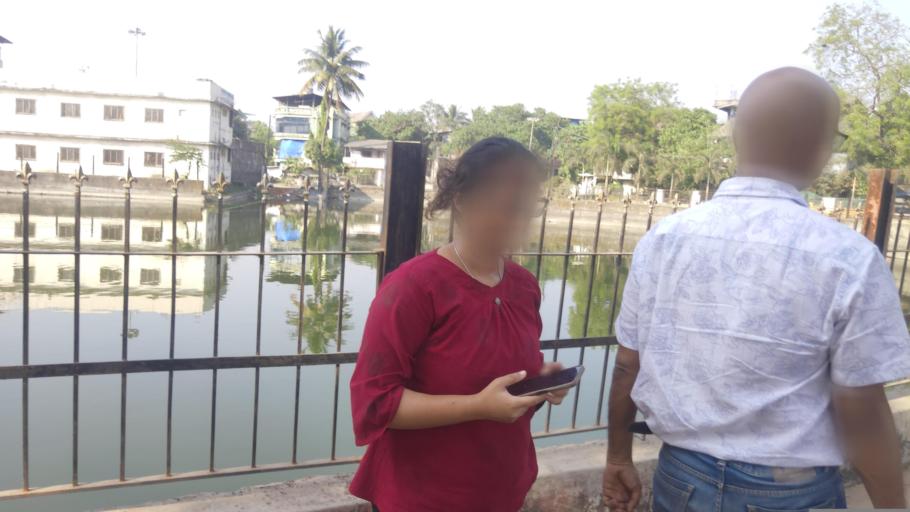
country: IN
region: Maharashtra
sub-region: Thane
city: Dombivli
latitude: 19.2456
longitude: 73.0361
